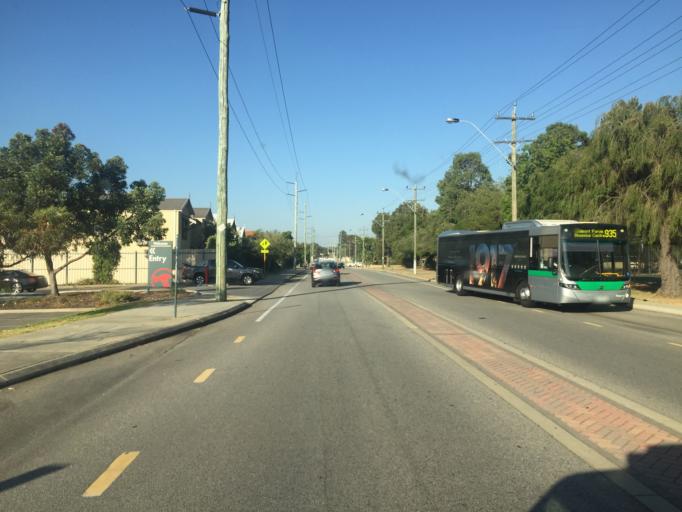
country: AU
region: Western Australia
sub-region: Belmont
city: Belmont
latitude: -31.9575
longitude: 115.9324
